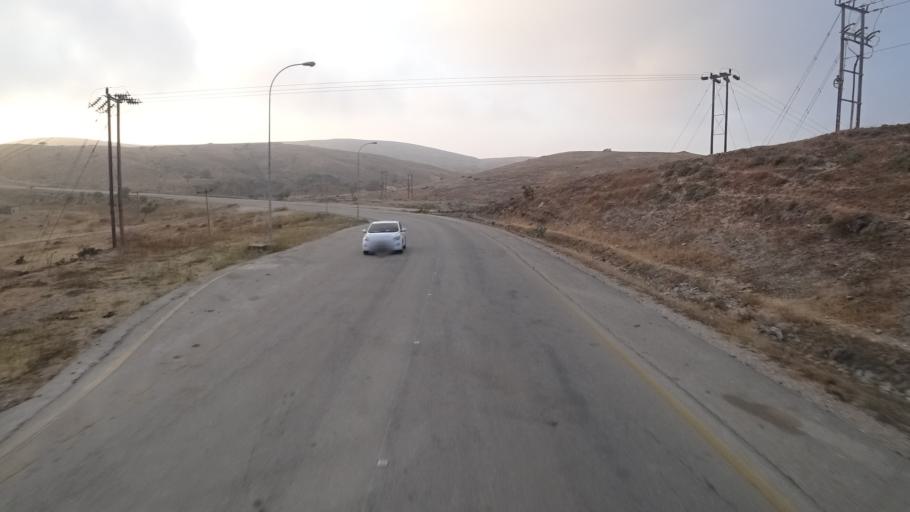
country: OM
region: Zufar
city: Salalah
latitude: 17.1394
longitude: 53.9704
